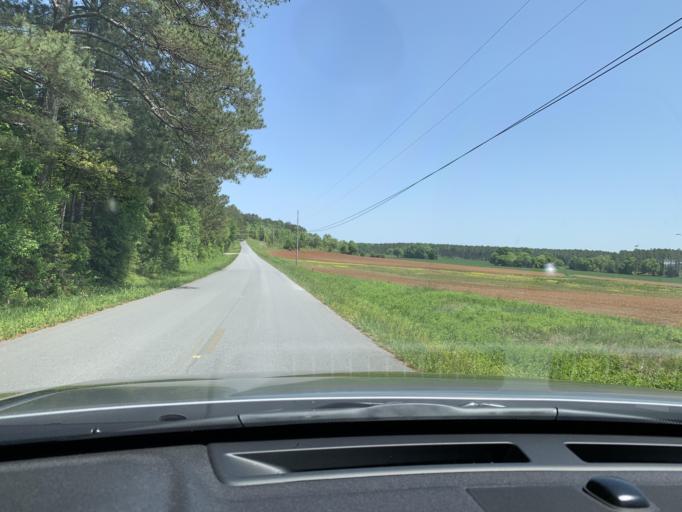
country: US
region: Georgia
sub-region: Polk County
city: Cedartown
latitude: 34.0404
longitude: -85.1908
